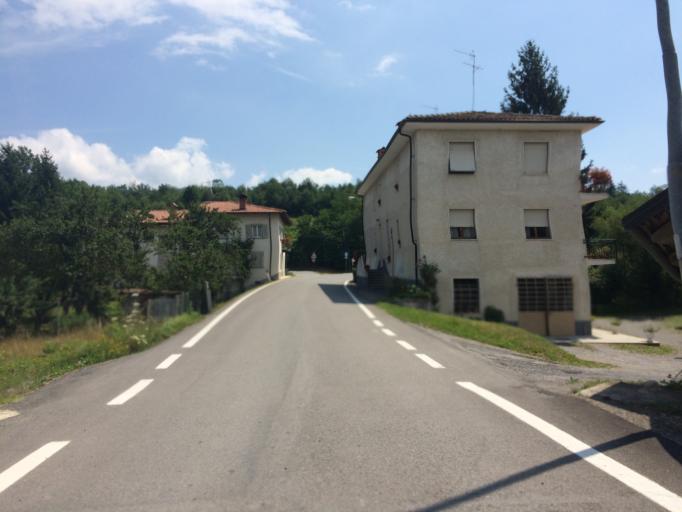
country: IT
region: Piedmont
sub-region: Provincia di Cuneo
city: Bagnasco
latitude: 44.3075
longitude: 8.0540
